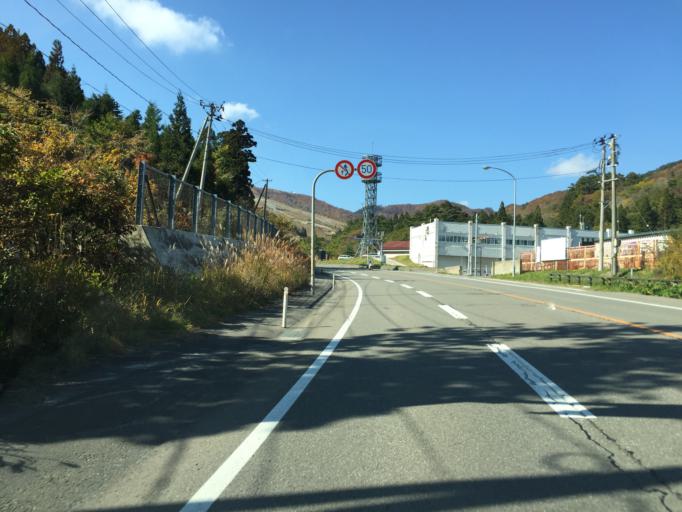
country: JP
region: Yamagata
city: Yonezawa
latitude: 37.8220
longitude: 140.2716
